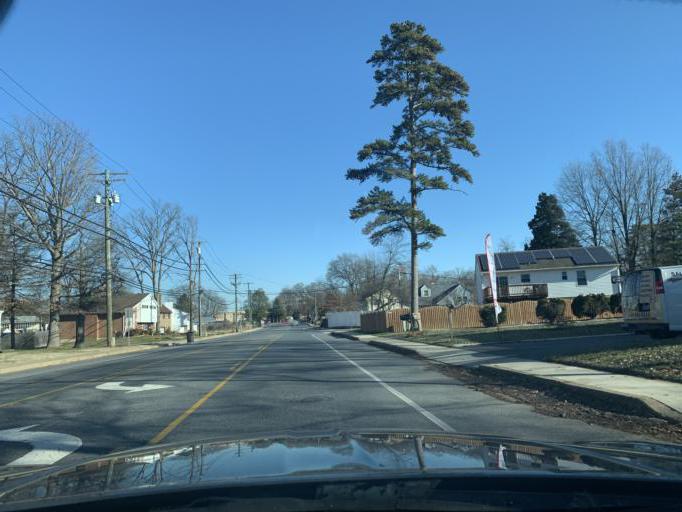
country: US
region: Maryland
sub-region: Anne Arundel County
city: Glen Burnie
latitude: 39.1511
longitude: -76.6232
